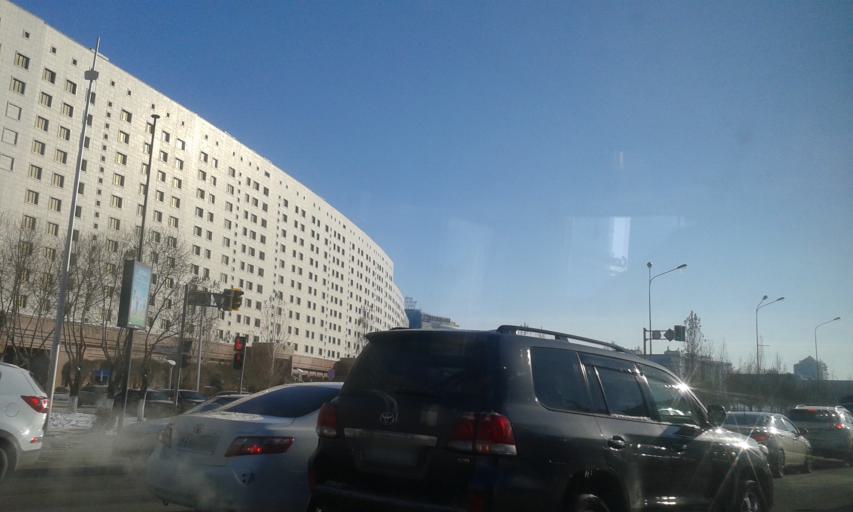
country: KZ
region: Astana Qalasy
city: Astana
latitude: 51.1255
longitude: 71.4386
